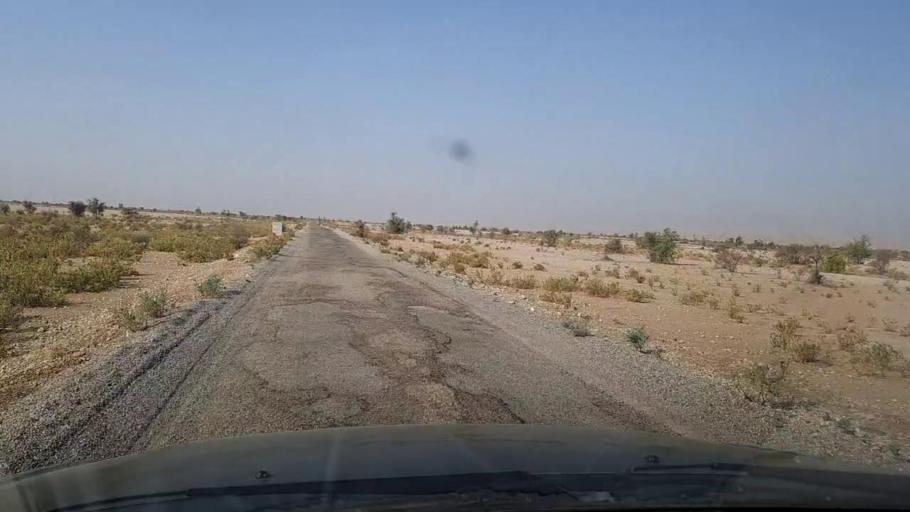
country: PK
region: Sindh
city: Sann
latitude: 25.9145
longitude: 68.0106
